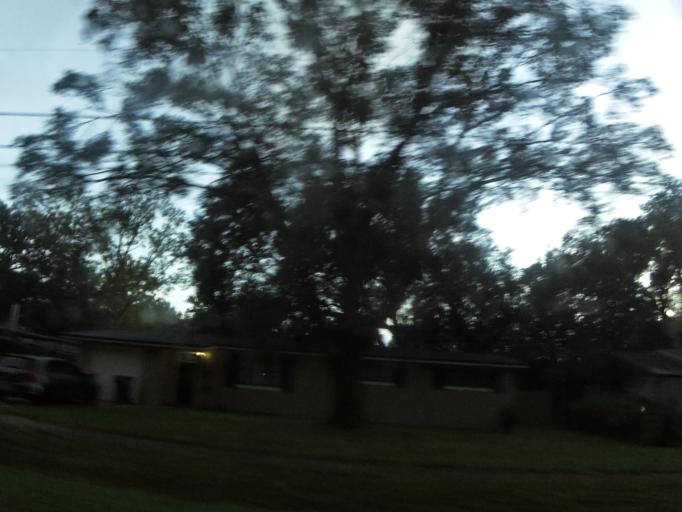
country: US
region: Florida
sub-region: Duval County
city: Jacksonville
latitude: 30.2465
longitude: -81.6177
